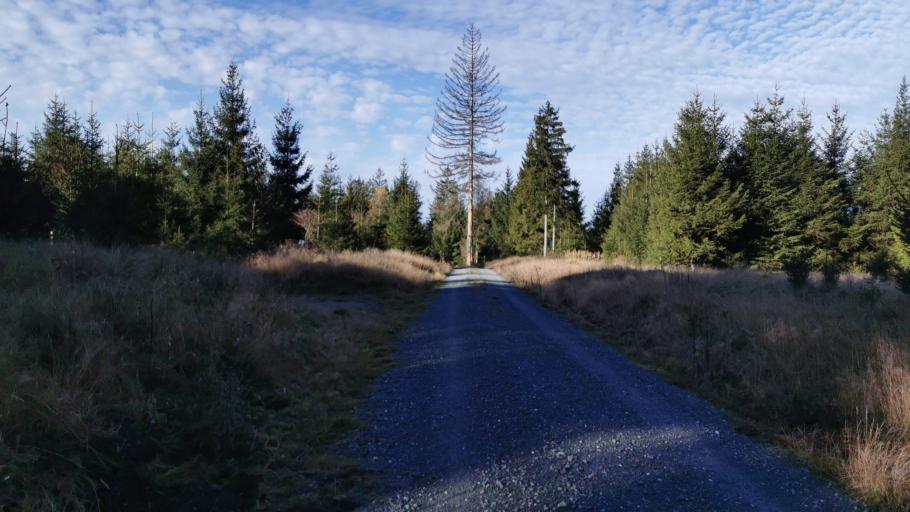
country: DE
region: Bavaria
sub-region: Upper Franconia
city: Tschirn
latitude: 50.4255
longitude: 11.4539
